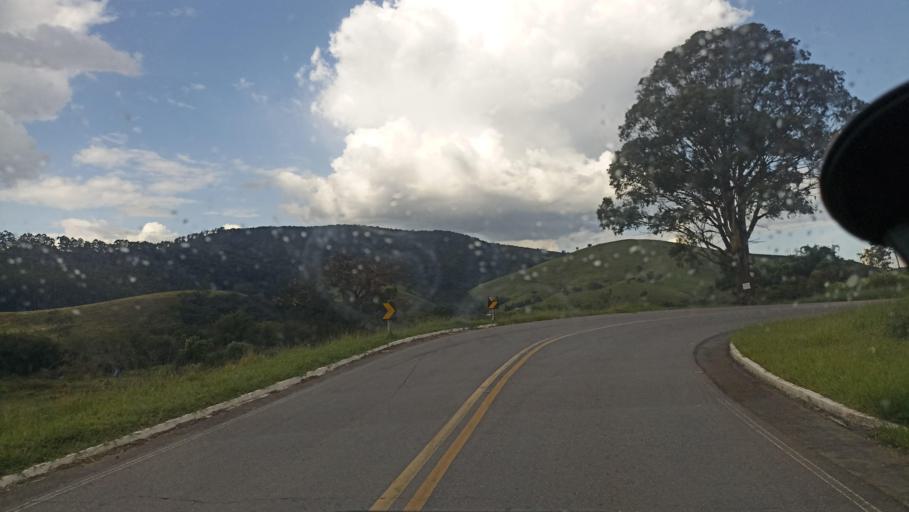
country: BR
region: Minas Gerais
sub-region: Baependi
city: Baependi
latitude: -21.9227
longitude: -44.8199
